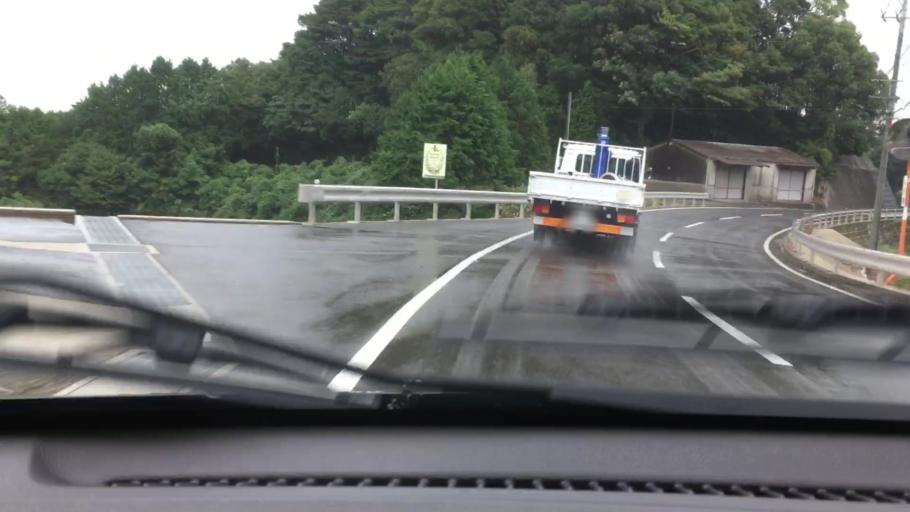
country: JP
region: Nagasaki
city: Togitsu
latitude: 32.8681
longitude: 129.7679
